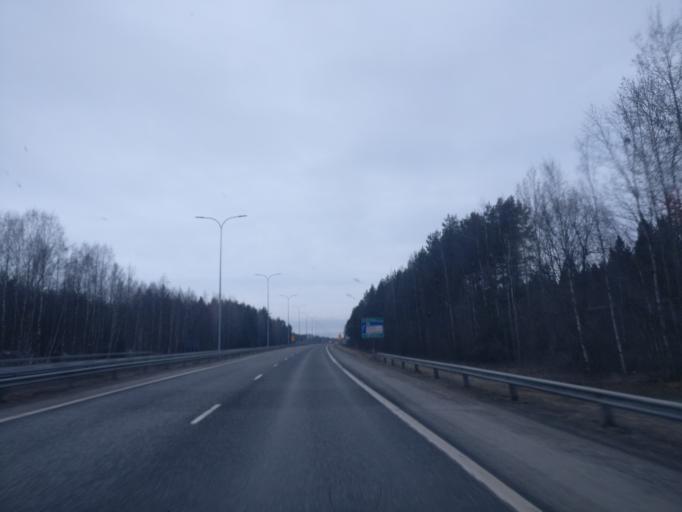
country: FI
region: Northern Ostrobothnia
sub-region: Oulu
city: Oulu
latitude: 65.0439
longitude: 25.4679
